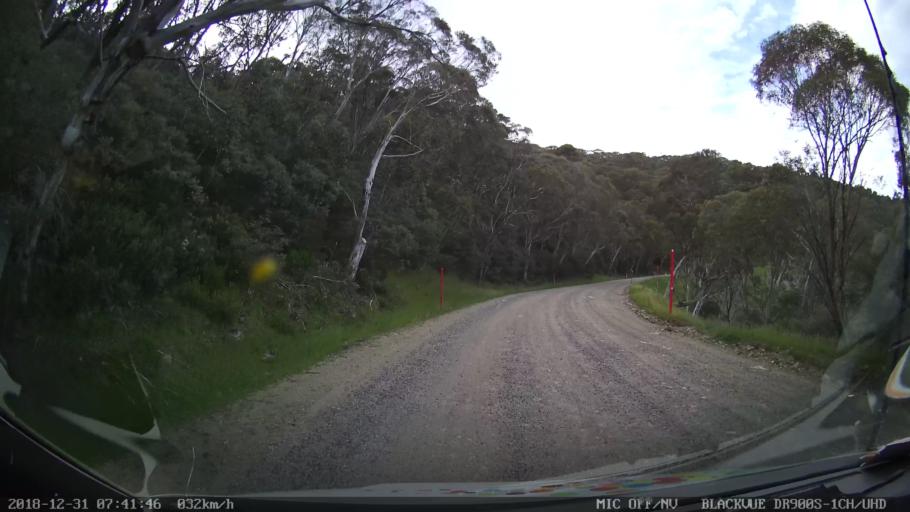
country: AU
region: New South Wales
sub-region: Snowy River
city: Jindabyne
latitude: -36.3546
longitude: 148.4117
